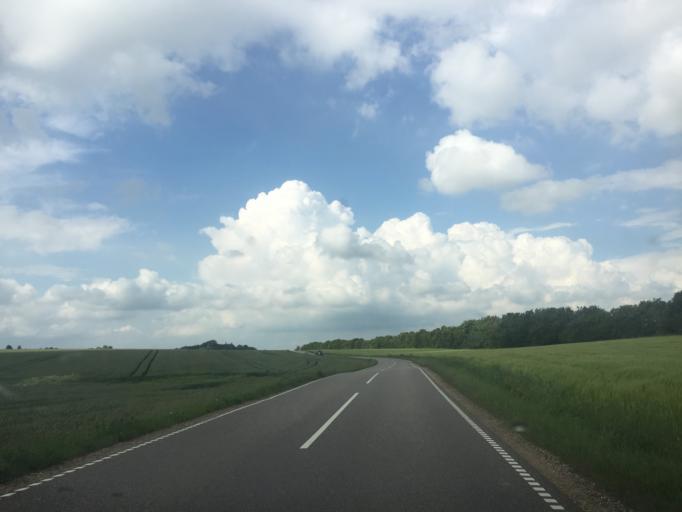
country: DK
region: Capital Region
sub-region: Hoje-Taastrup Kommune
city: Flong
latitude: 55.6818
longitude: 12.1882
